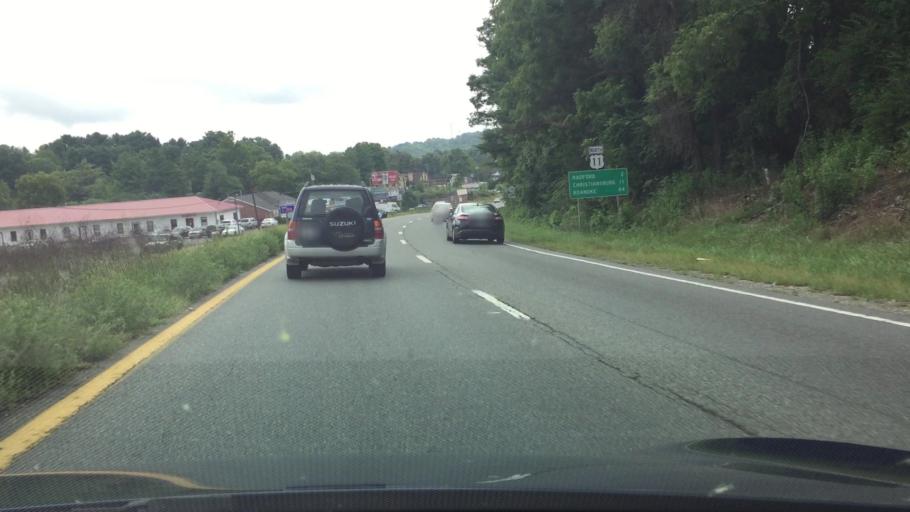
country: US
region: Virginia
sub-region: Pulaski County
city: Fairlawn
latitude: 37.1465
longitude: -80.5861
